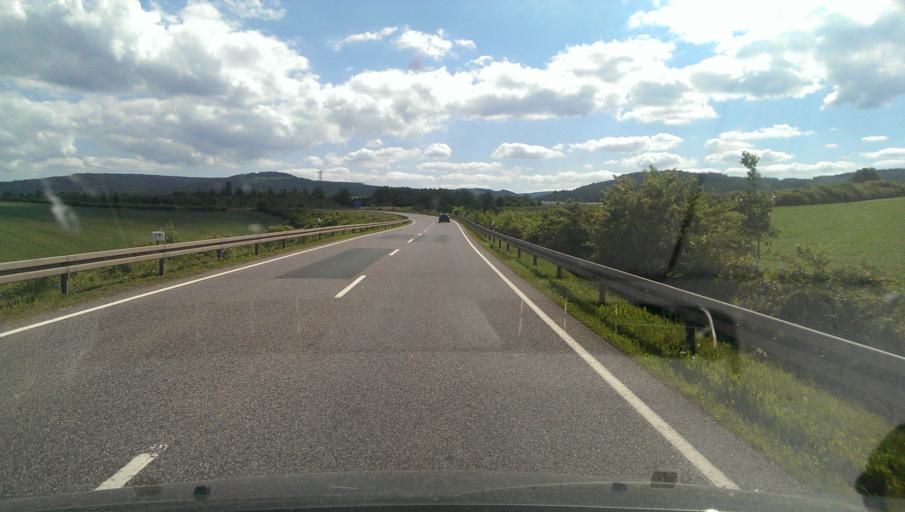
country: DE
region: Thuringia
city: Geschwenda
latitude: 50.7303
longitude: 10.8357
